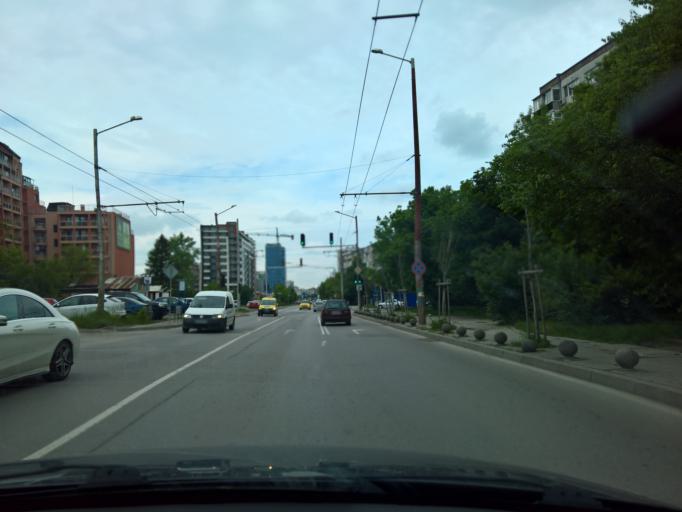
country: BG
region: Sofia-Capital
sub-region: Stolichna Obshtina
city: Sofia
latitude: 42.6615
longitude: 23.2957
